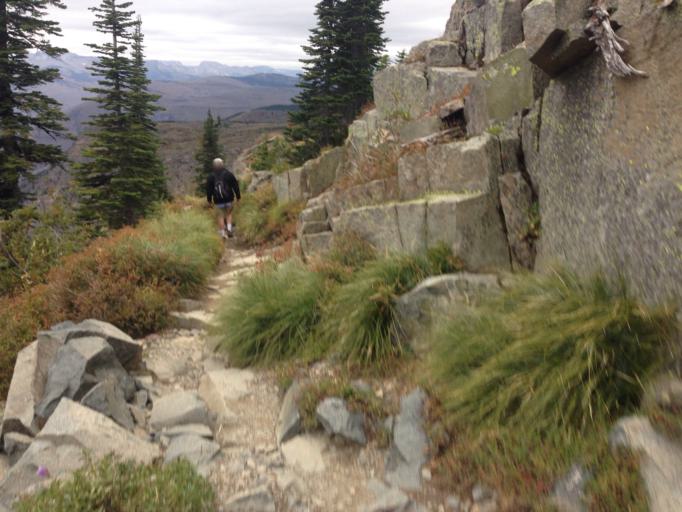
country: US
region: Montana
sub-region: Flathead County
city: Columbia Falls
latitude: 48.7460
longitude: -113.7455
